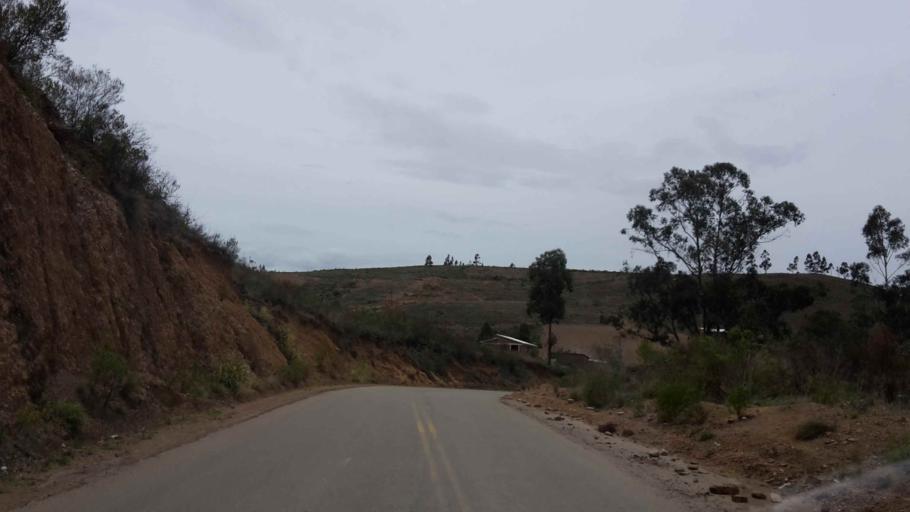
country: BO
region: Cochabamba
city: Totora
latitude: -17.7233
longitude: -65.1957
